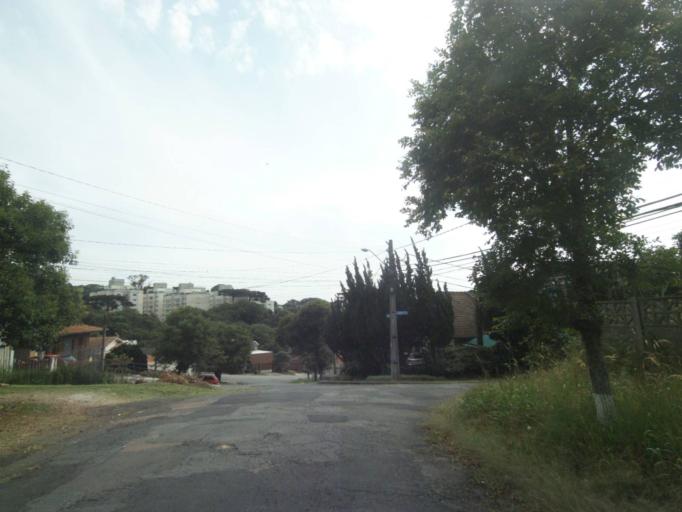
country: BR
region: Parana
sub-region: Curitiba
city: Curitiba
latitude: -25.4128
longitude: -49.2981
